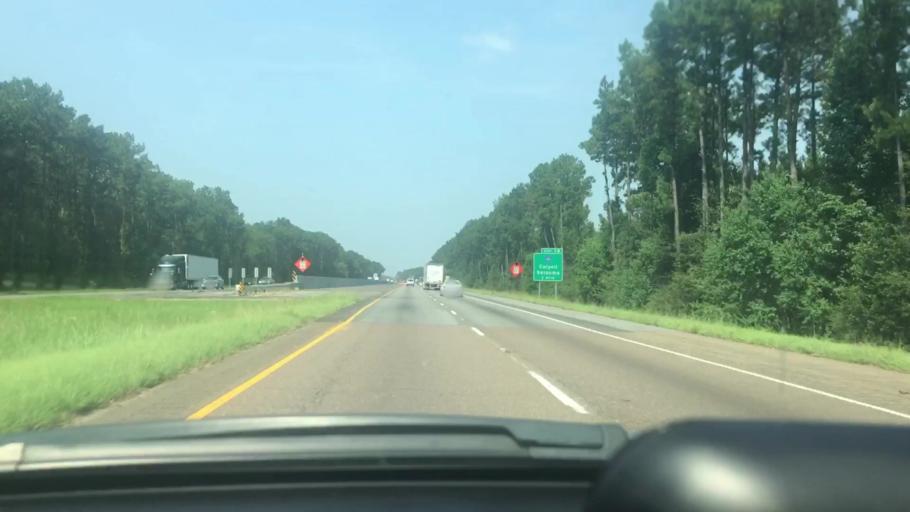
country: US
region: Louisiana
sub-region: Livingston Parish
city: Livingston
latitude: 30.4741
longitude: -90.7758
